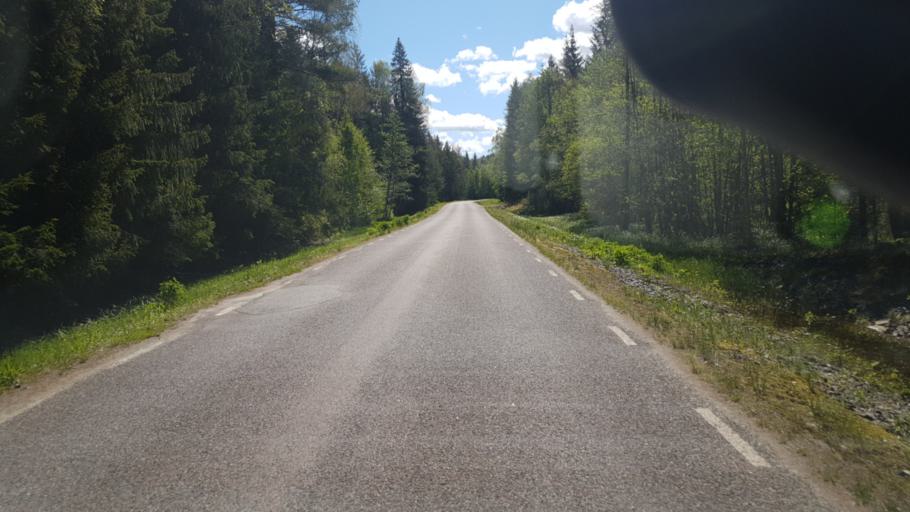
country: SE
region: Vaermland
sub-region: Arvika Kommun
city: Arvika
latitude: 59.5164
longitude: 12.8500
